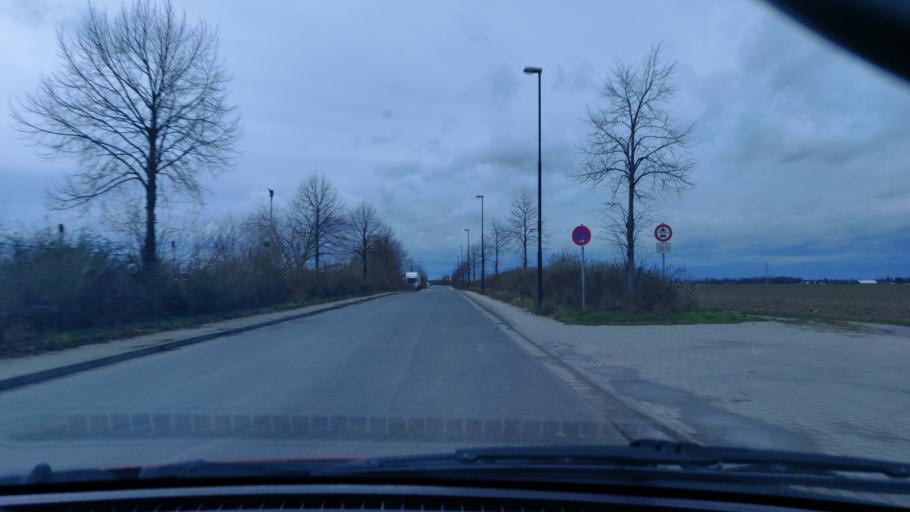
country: DE
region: North Rhine-Westphalia
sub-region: Regierungsbezirk Koln
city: Kerpen
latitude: 50.8970
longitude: 6.6517
